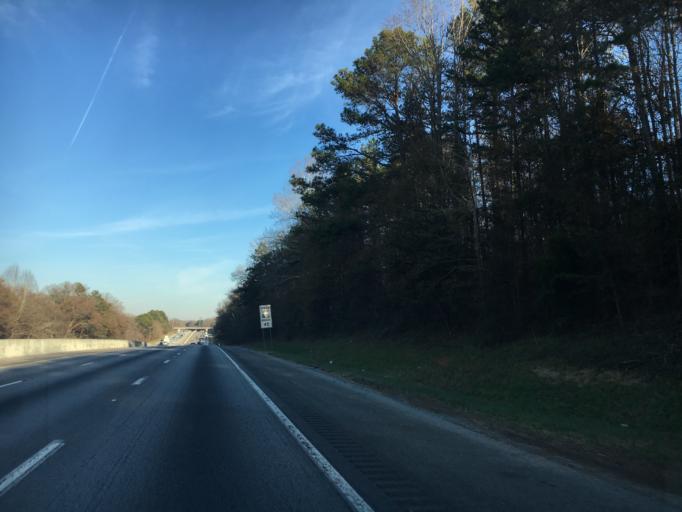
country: US
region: South Carolina
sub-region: Anderson County
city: Northlake
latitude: 34.6033
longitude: -82.6448
